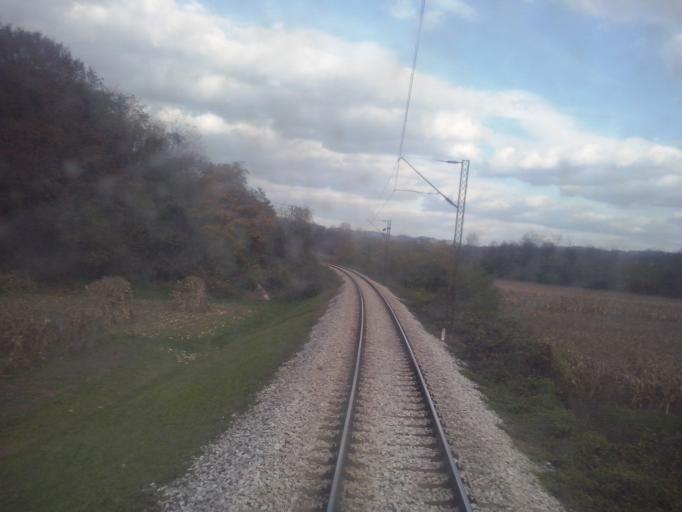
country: RS
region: Central Serbia
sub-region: Zlatiborski Okrug
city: Pozega
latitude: 43.8075
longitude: 20.0267
